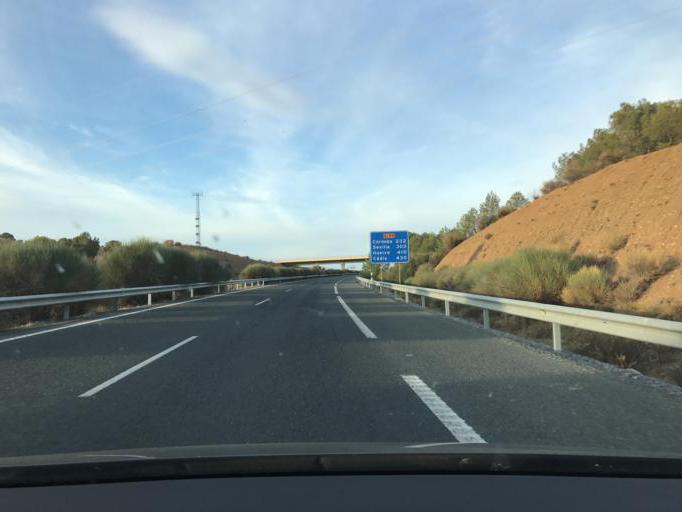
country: ES
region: Andalusia
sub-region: Provincia de Granada
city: Guadix
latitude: 37.2693
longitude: -3.0948
